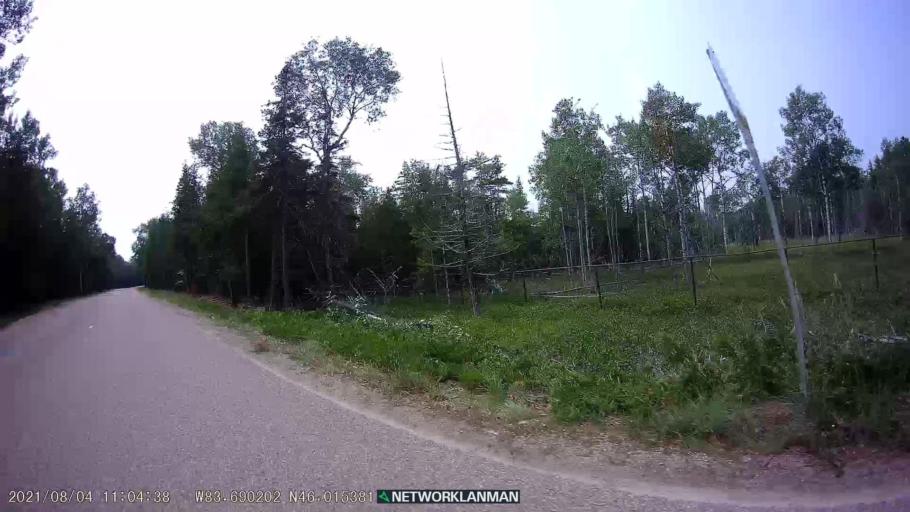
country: CA
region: Ontario
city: Thessalon
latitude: 46.0151
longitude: -83.6904
